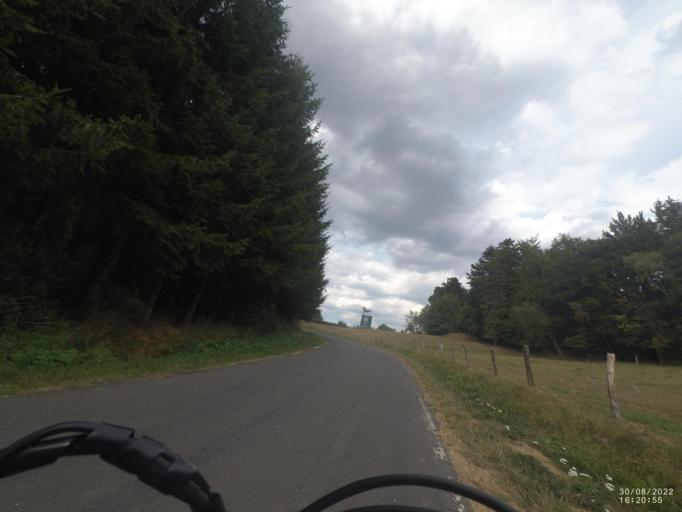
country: DE
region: Rheinland-Pfalz
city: Ormont
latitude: 50.3243
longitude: 6.4482
